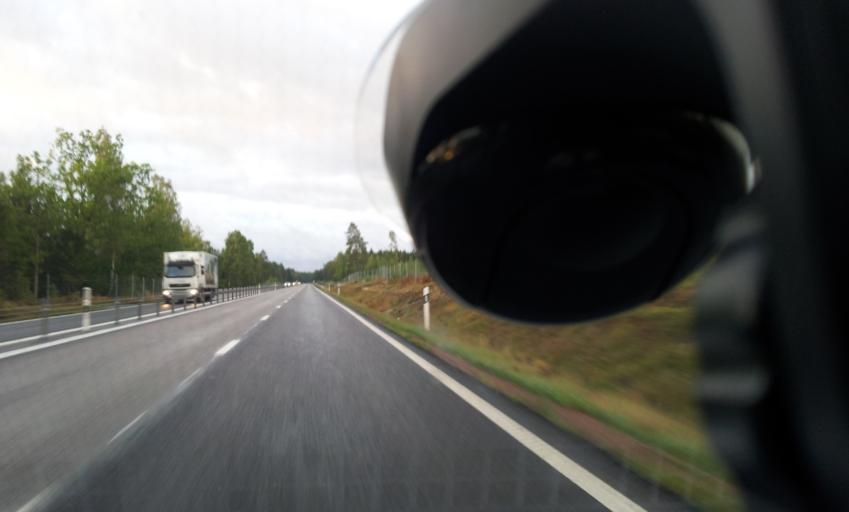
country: SE
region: Kalmar
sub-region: Monsteras Kommun
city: Timmernabben
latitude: 56.8825
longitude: 16.3826
